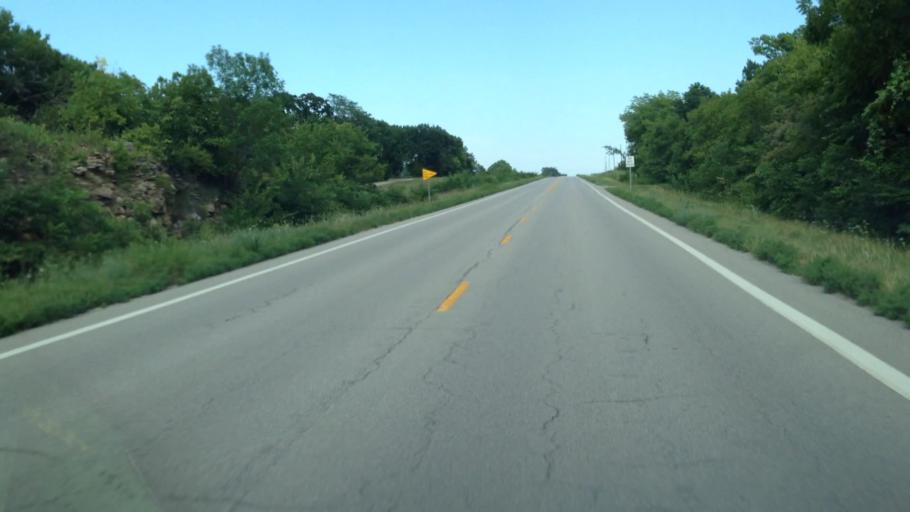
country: US
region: Kansas
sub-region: Neosho County
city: Erie
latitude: 37.6885
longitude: -95.1962
